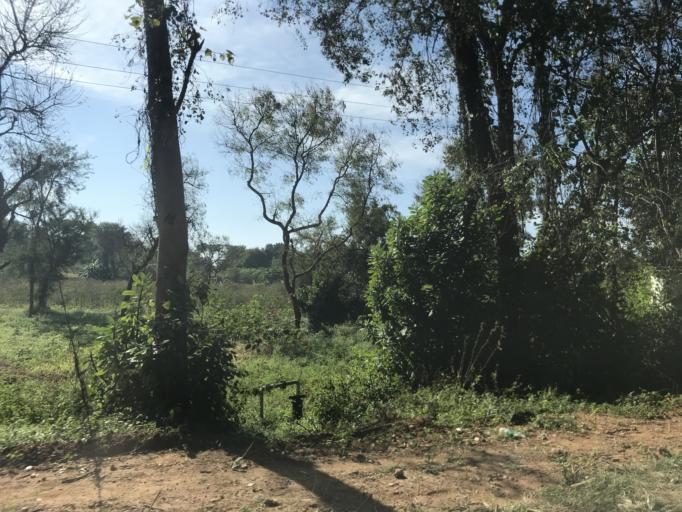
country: IN
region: Karnataka
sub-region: Mysore
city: Mysore
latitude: 12.2165
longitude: 76.5680
